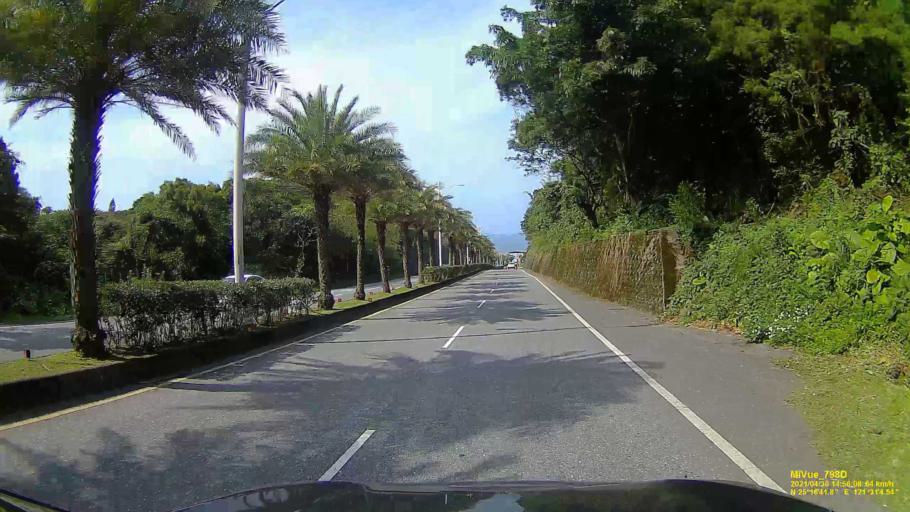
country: TW
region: Taipei
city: Taipei
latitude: 25.2787
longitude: 121.5181
